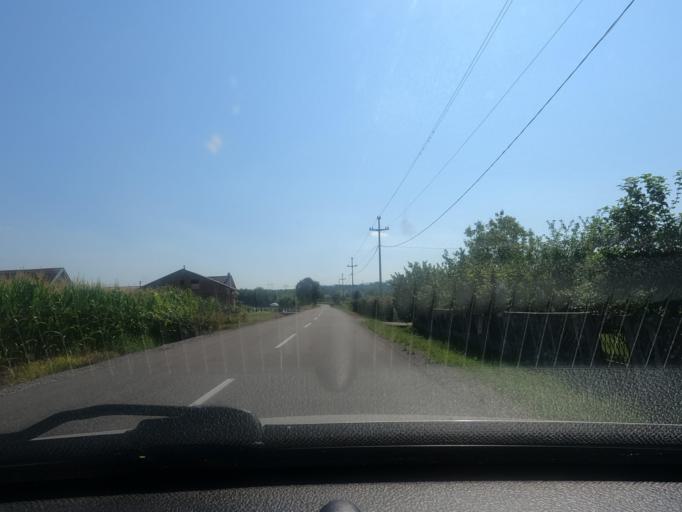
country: RS
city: Kozjak
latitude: 44.5512
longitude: 19.3118
